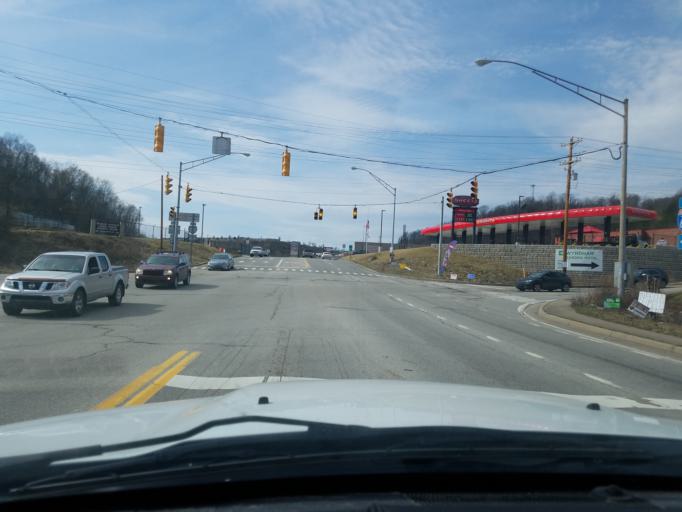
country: US
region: West Virginia
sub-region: Kanawha County
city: Cross Lanes
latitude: 38.4123
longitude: -81.7983
